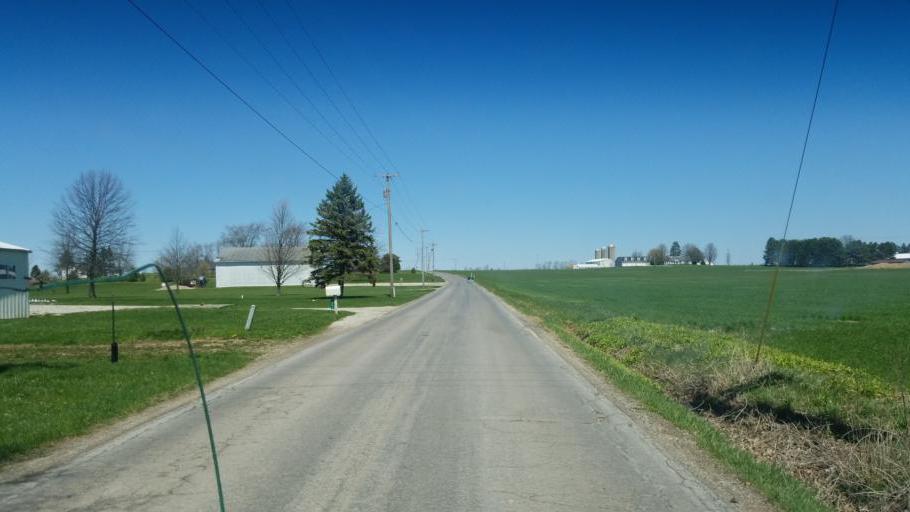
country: US
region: Ohio
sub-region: Huron County
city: Plymouth
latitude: 40.9708
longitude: -82.5825
